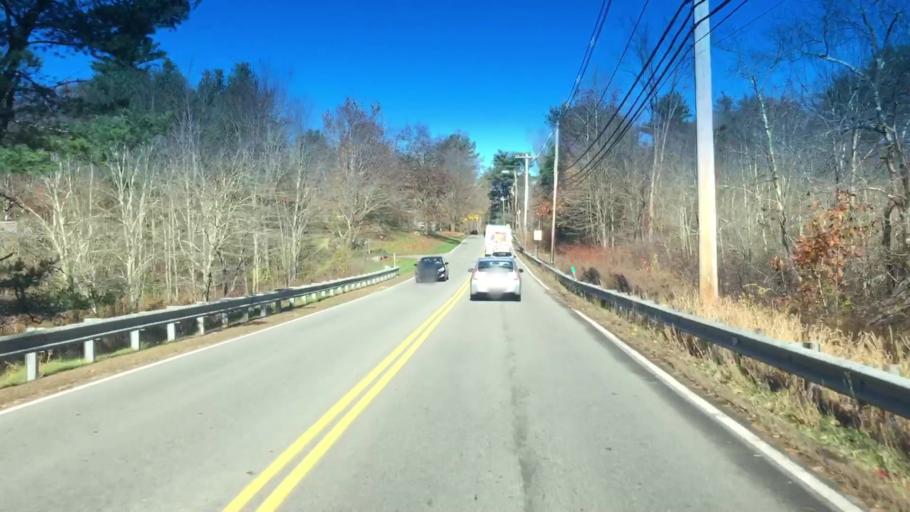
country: US
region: Massachusetts
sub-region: Norfolk County
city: Medfield
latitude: 42.1748
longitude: -71.2992
